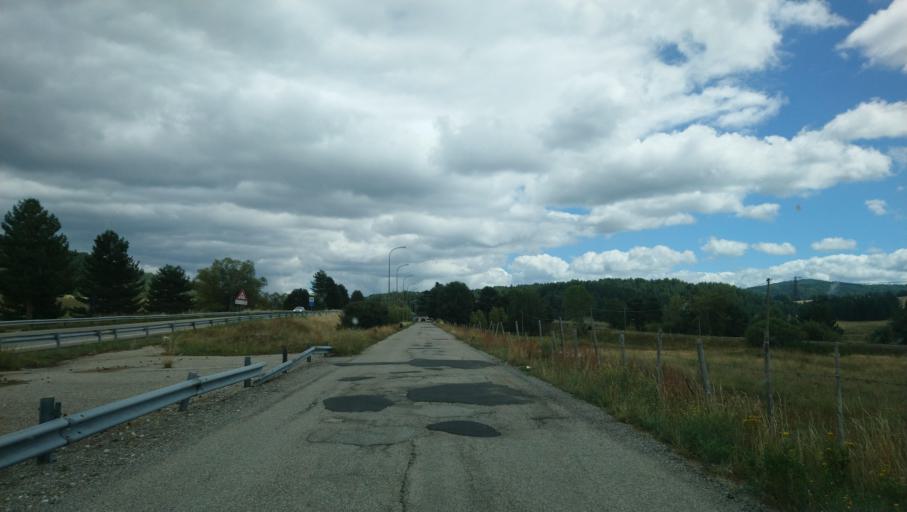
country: IT
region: Calabria
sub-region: Provincia di Cosenza
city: Longobucco
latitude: 39.3157
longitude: 16.5478
